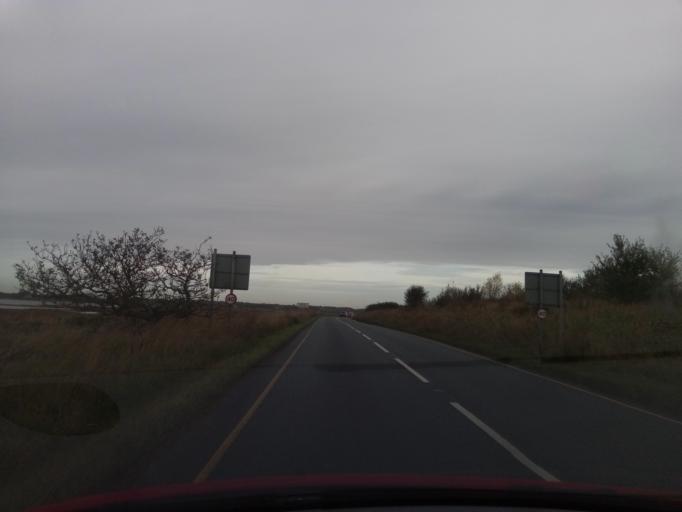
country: GB
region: England
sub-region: Essex
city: West Mersea
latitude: 51.7932
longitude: 0.9212
